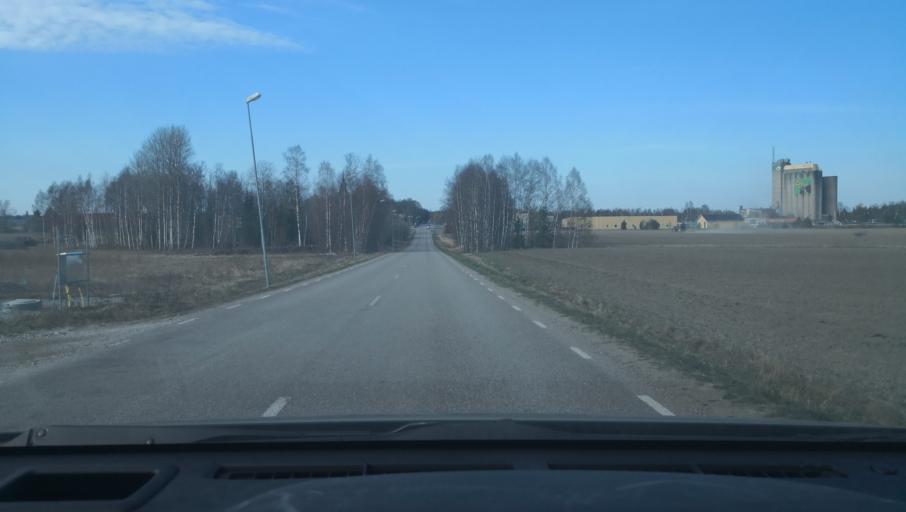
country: SE
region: Uppsala
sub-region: Heby Kommun
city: Heby
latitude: 59.9318
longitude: 16.8564
